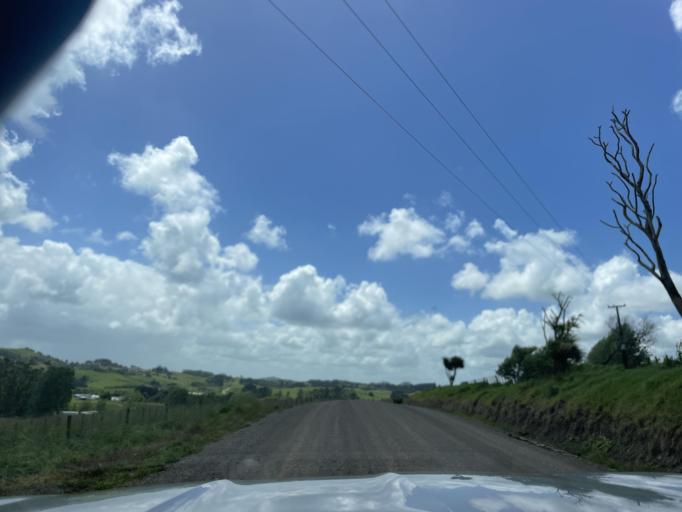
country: NZ
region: Auckland
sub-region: Auckland
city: Wellsford
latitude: -36.1678
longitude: 174.3206
